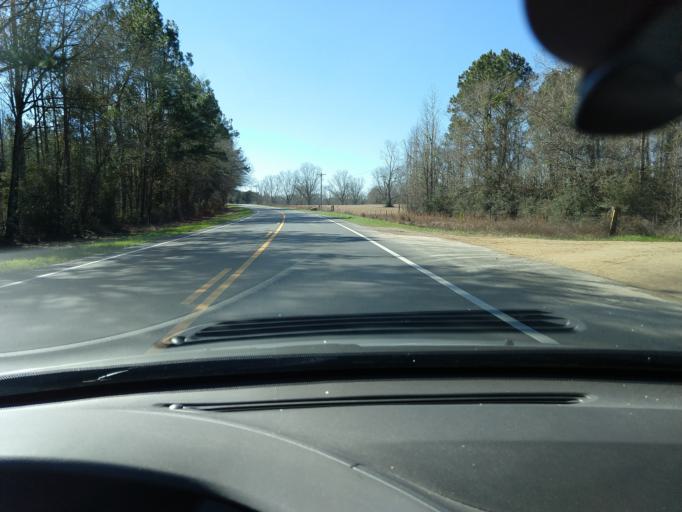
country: US
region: Alabama
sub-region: Covington County
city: Andalusia
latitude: 31.1891
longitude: -86.5716
